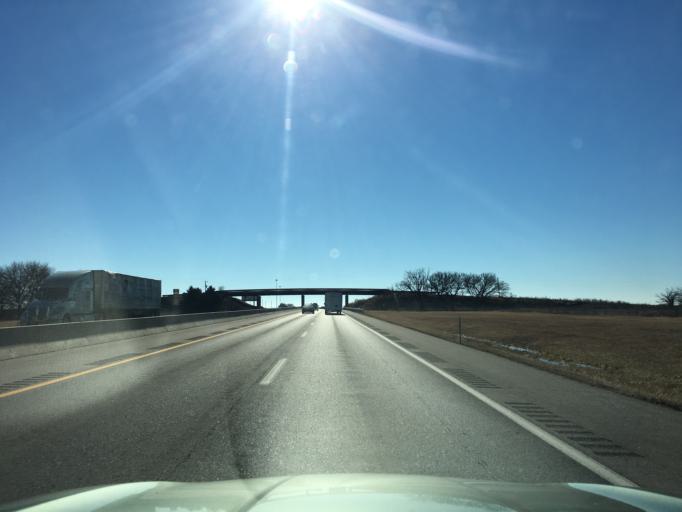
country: US
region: Oklahoma
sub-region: Kay County
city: Blackwell
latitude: 37.0302
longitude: -97.3383
